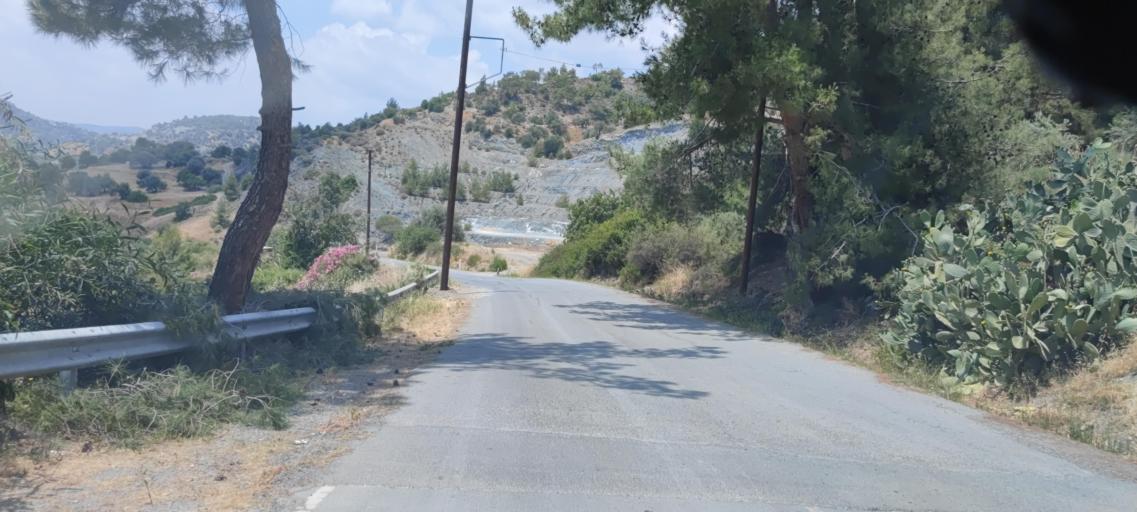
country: CY
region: Limassol
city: Pano Polemidia
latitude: 34.8013
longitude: 33.0119
